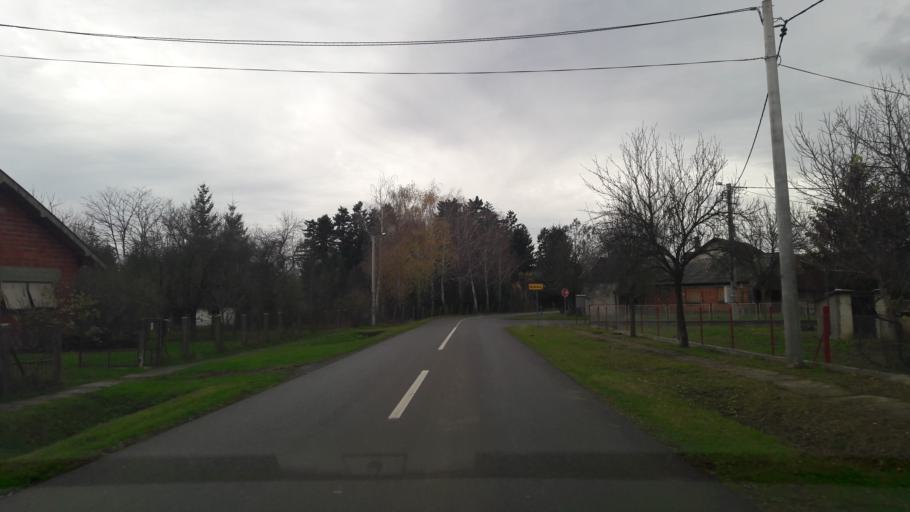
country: HR
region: Osjecko-Baranjska
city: Martin
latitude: 45.5310
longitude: 18.0525
